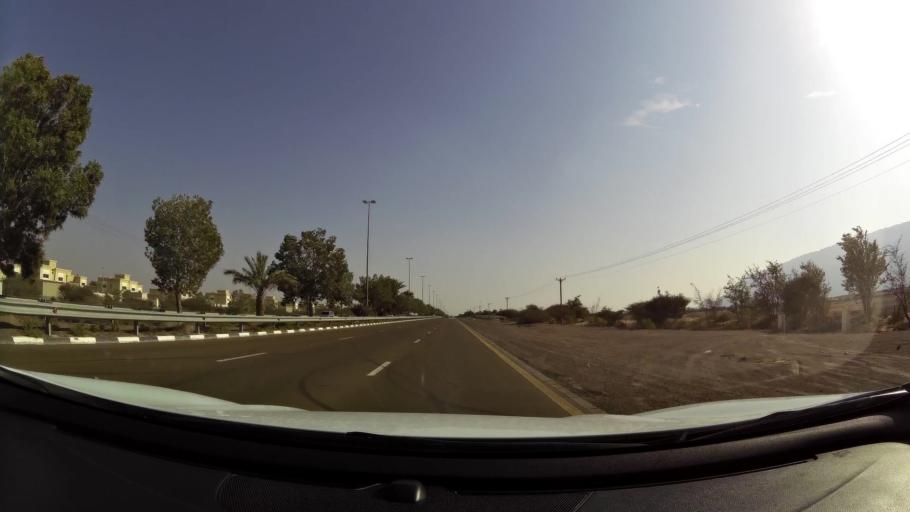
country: AE
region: Abu Dhabi
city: Al Ain
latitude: 24.0586
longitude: 55.8388
